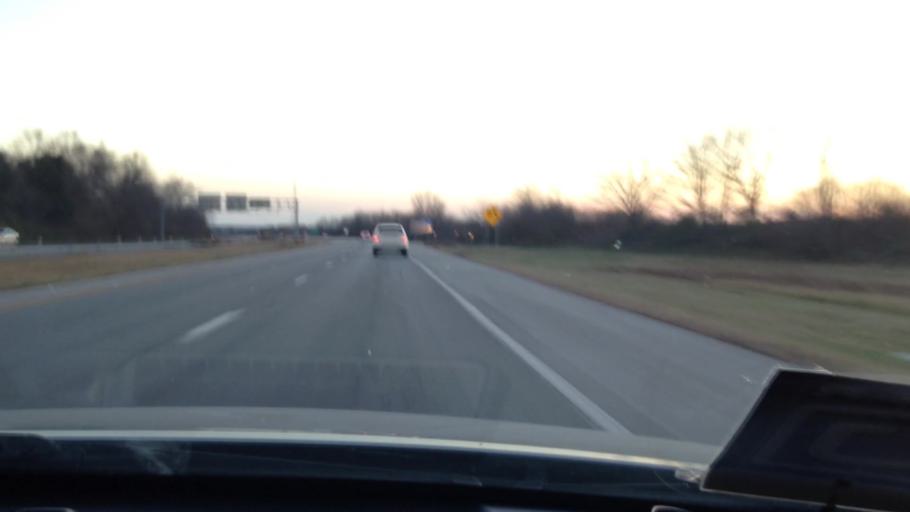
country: US
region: Missouri
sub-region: Clay County
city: Gladstone
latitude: 39.2563
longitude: -94.5892
